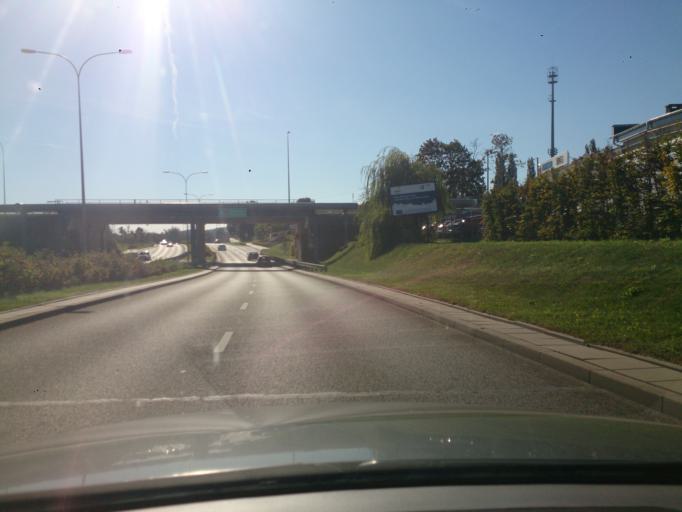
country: PL
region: Pomeranian Voivodeship
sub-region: Gdynia
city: Gdynia
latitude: 54.4927
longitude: 18.5368
